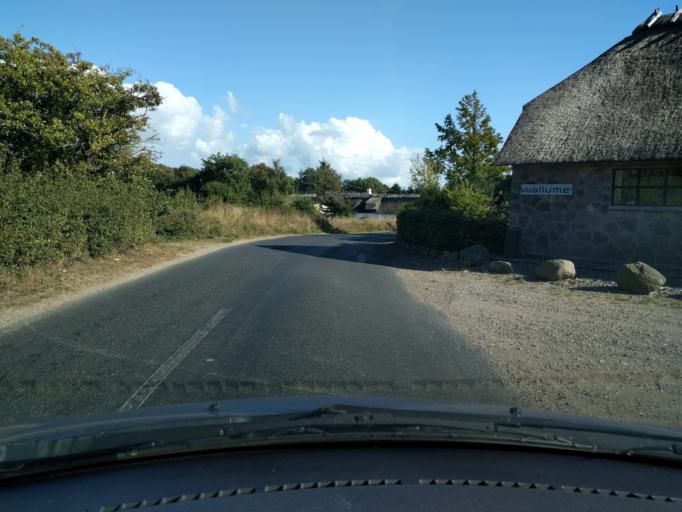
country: DK
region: South Denmark
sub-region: Assens Kommune
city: Harby
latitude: 55.1528
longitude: 10.0152
